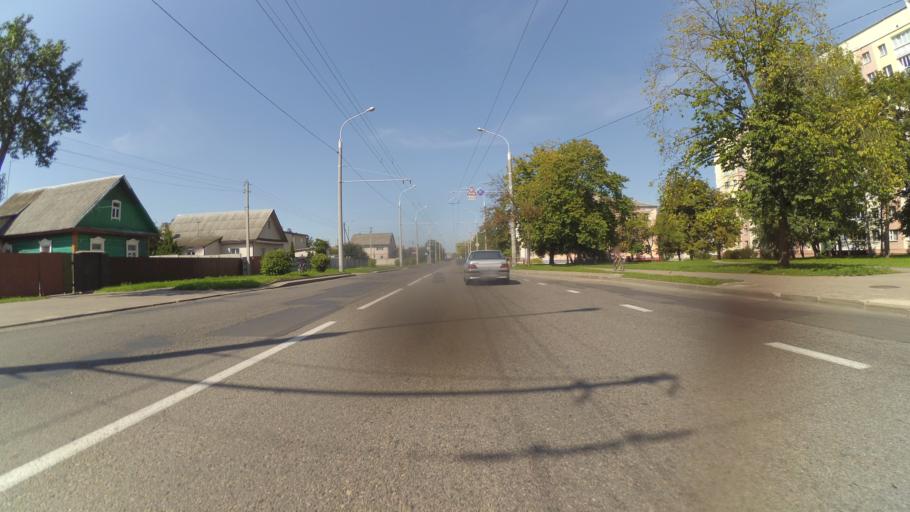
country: BY
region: Minsk
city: Vyaliki Trastsyanets
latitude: 53.8752
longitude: 27.6824
